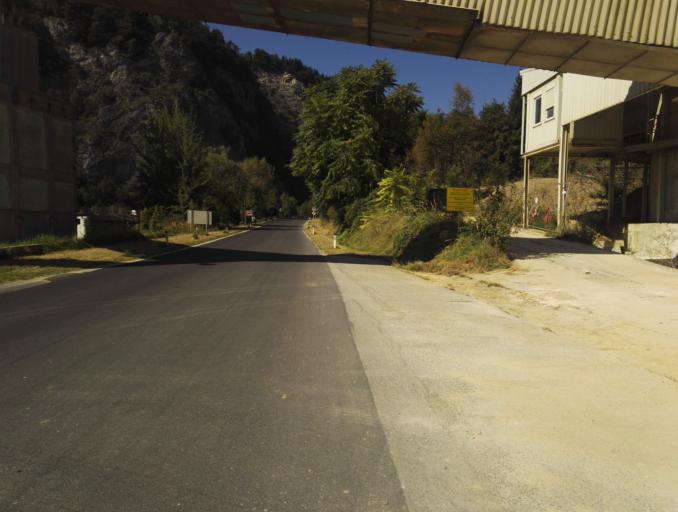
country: AT
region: Styria
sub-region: Politischer Bezirk Graz-Umgebung
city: Peggau
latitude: 47.2169
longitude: 15.3402
